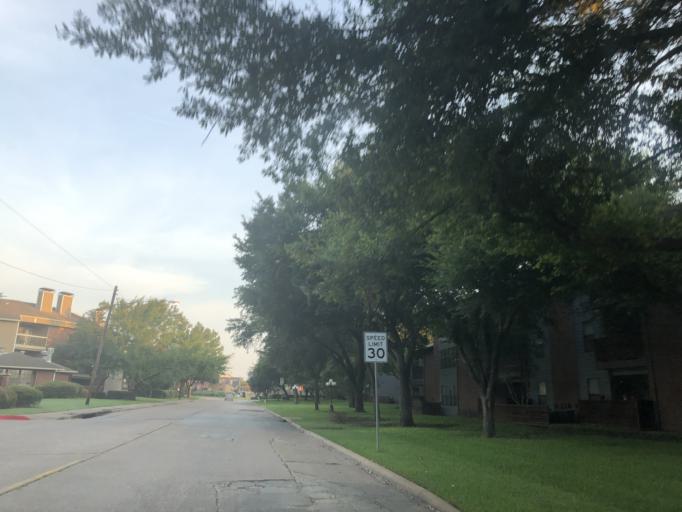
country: US
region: Texas
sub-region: Dallas County
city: Garland
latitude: 32.8466
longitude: -96.6401
